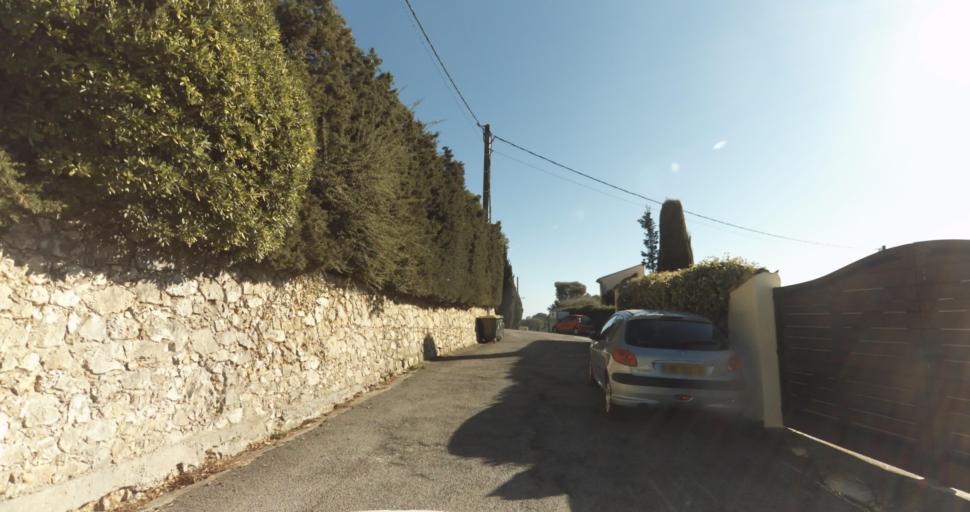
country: FR
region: Provence-Alpes-Cote d'Azur
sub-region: Departement des Alpes-Maritimes
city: Vence
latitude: 43.7193
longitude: 7.1017
